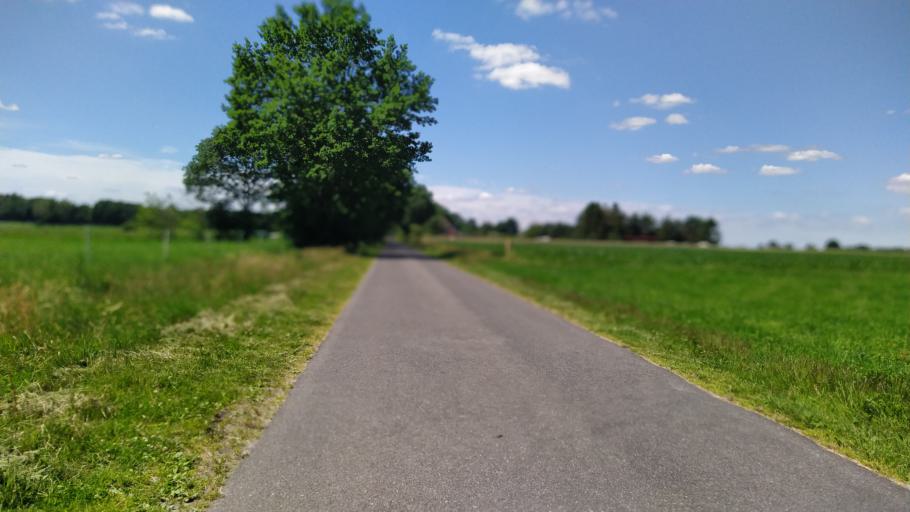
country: DE
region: Lower Saxony
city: Heinbockel
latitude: 53.5471
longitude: 9.3052
